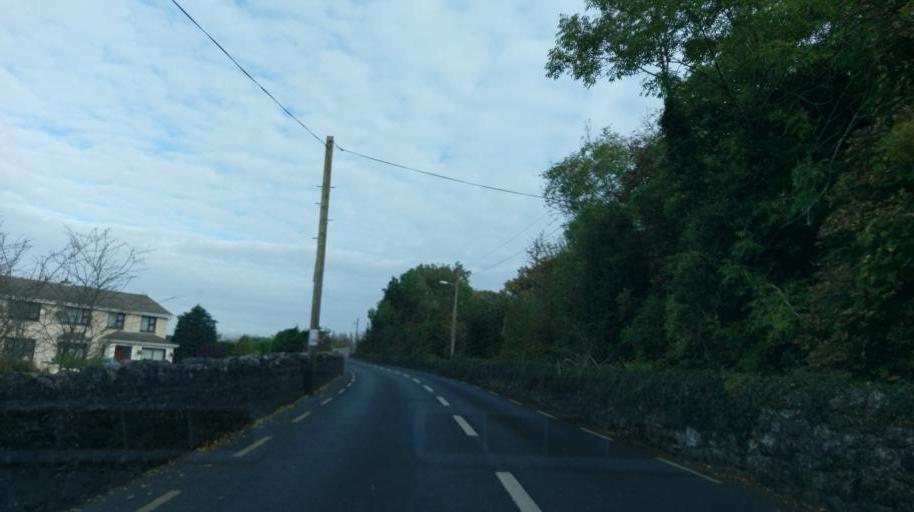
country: IE
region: Connaught
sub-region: County Galway
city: Athenry
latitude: 53.3042
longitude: -8.7423
